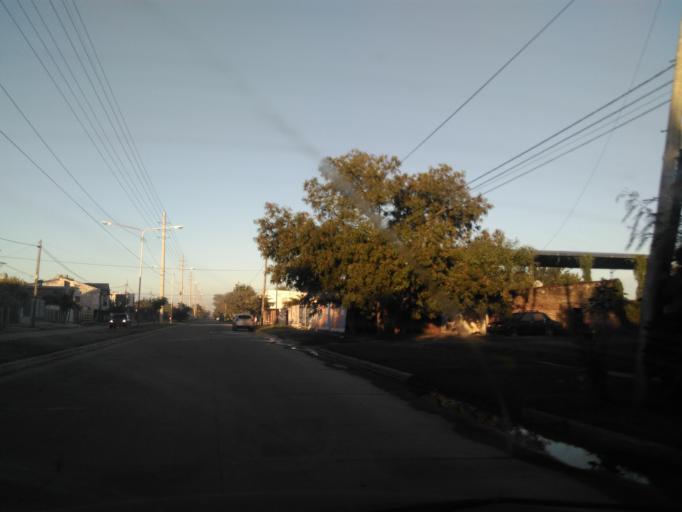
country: AR
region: Chaco
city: Resistencia
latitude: -27.4701
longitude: -58.9991
